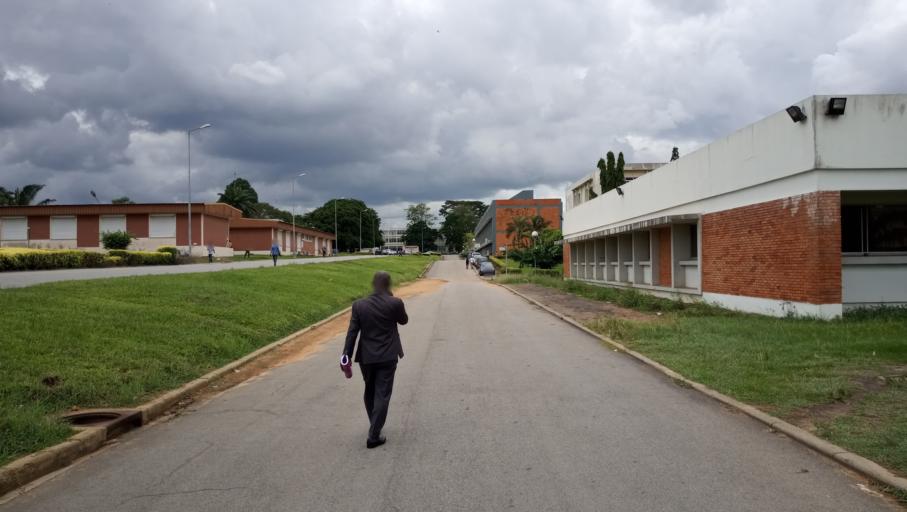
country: CI
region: Lagunes
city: Abidjan
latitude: 5.3404
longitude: -3.9865
